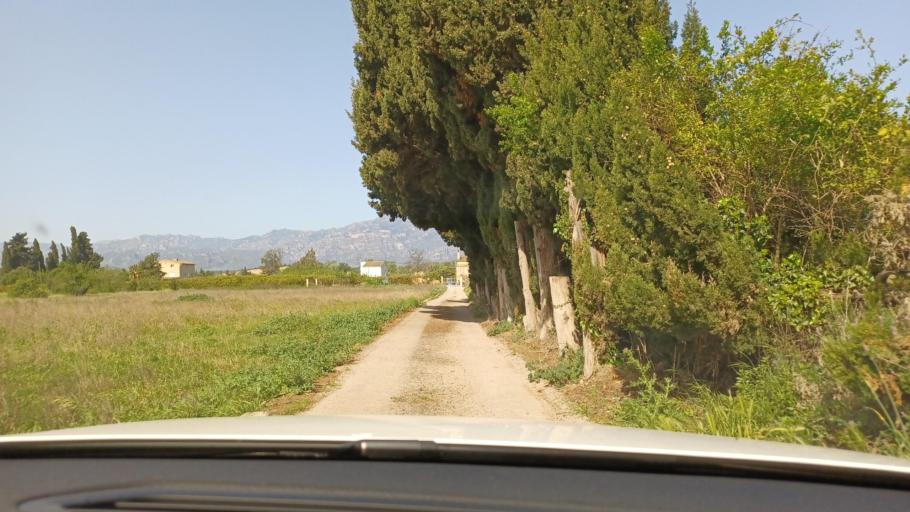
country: ES
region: Catalonia
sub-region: Provincia de Tarragona
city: Tortosa
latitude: 40.7926
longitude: 0.5137
